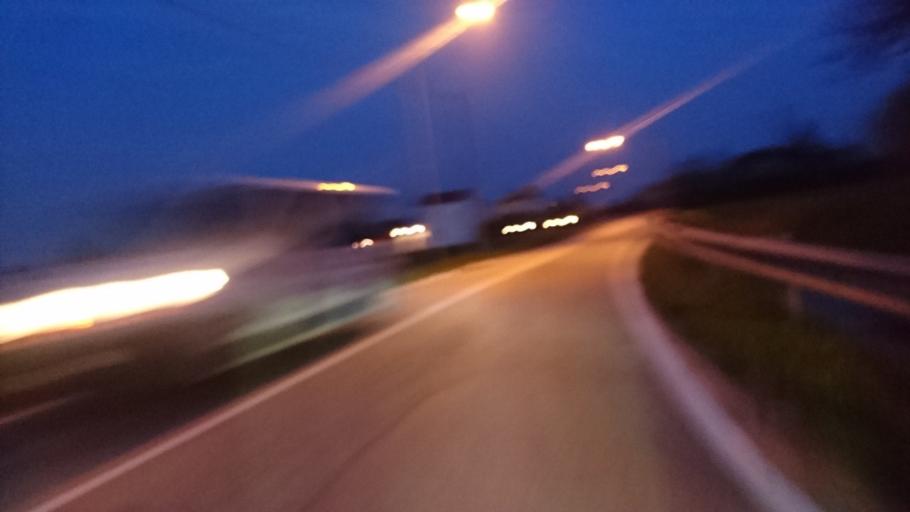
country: IT
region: Veneto
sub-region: Provincia di Padova
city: Selvazzano Dentro
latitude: 45.3719
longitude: 11.7988
